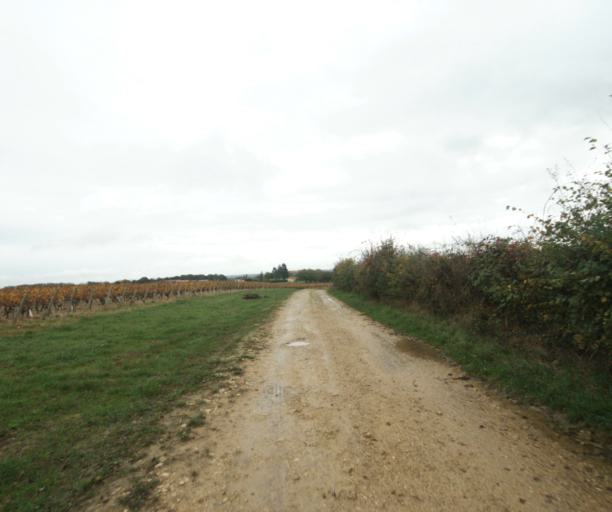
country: FR
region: Bourgogne
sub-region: Departement de Saone-et-Loire
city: Tournus
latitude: 46.4864
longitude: 4.8623
